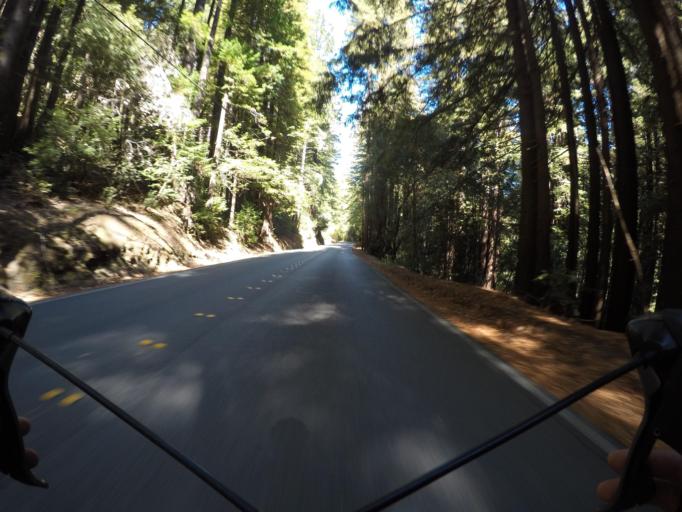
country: US
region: California
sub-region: San Mateo County
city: Portola Valley
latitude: 37.2986
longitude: -122.2664
